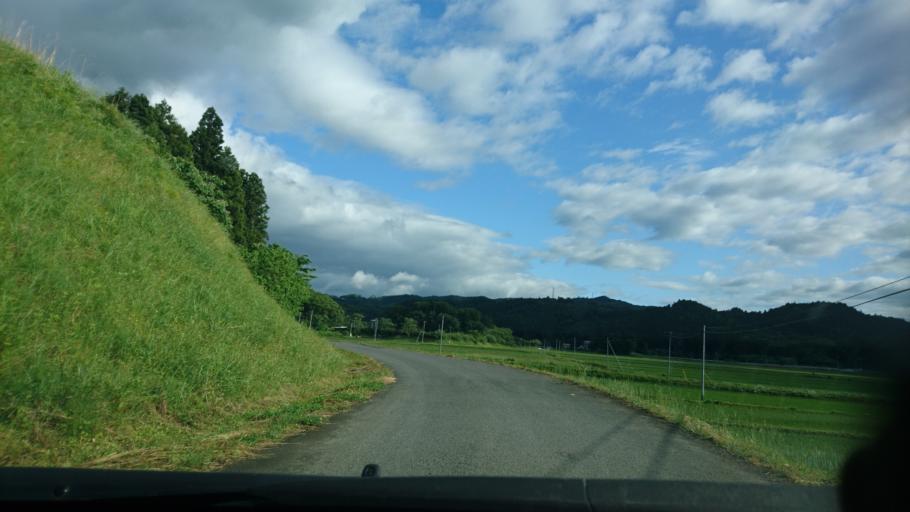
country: JP
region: Iwate
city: Ichinoseki
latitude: 38.8555
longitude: 141.2872
